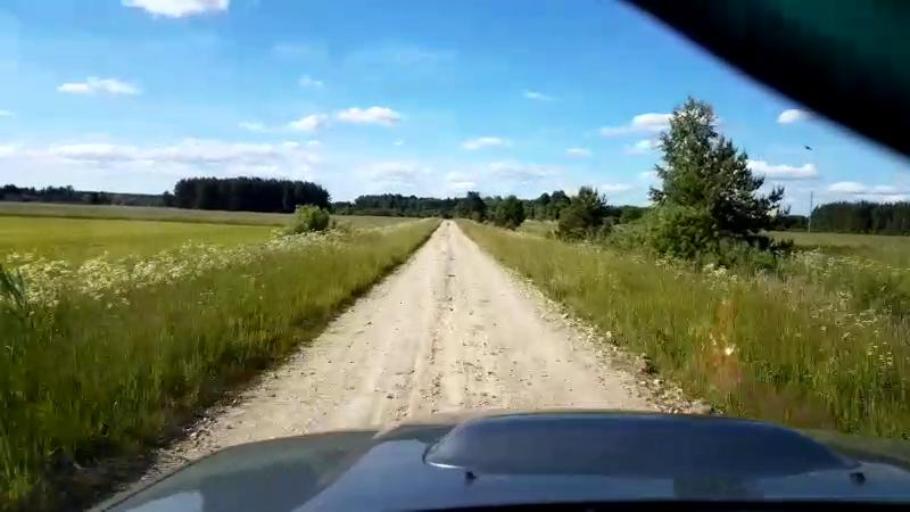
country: EE
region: Paernumaa
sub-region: Sauga vald
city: Sauga
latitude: 58.5066
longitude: 24.5902
